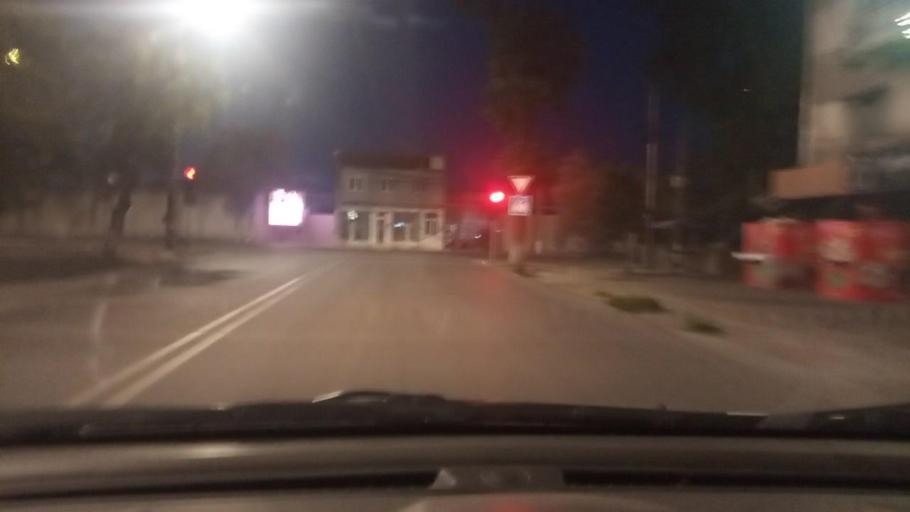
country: UZ
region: Toshkent Shahri
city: Tashkent
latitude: 41.2724
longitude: 69.2790
